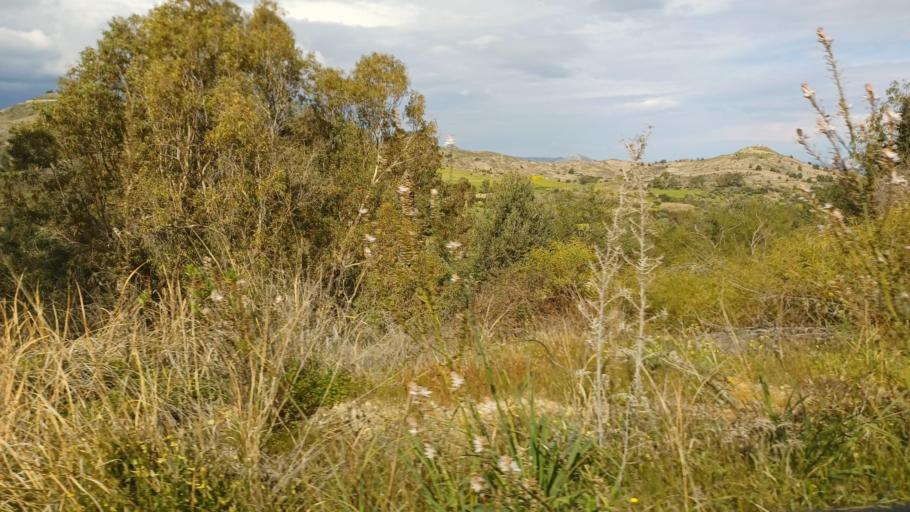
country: CY
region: Lefkosia
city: Lefka
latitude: 35.1004
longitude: 32.8861
